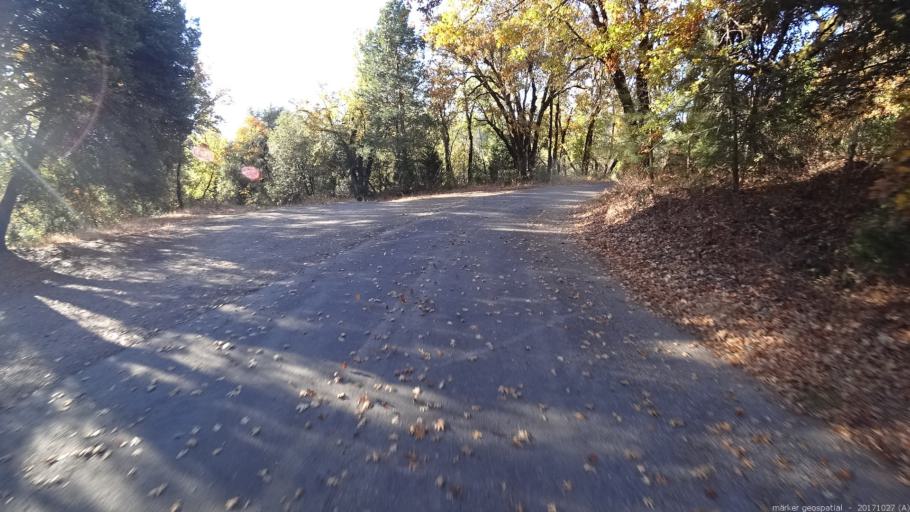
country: US
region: California
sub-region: Shasta County
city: Burney
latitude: 41.0226
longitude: -121.9045
